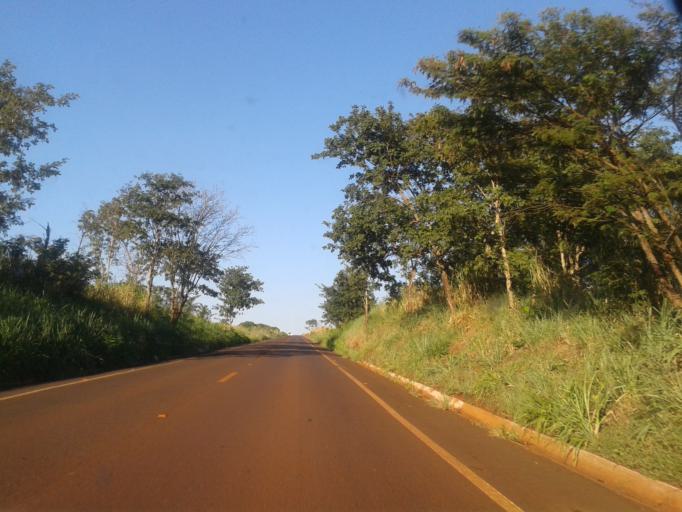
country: BR
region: Minas Gerais
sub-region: Capinopolis
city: Capinopolis
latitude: -18.7076
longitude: -49.7011
